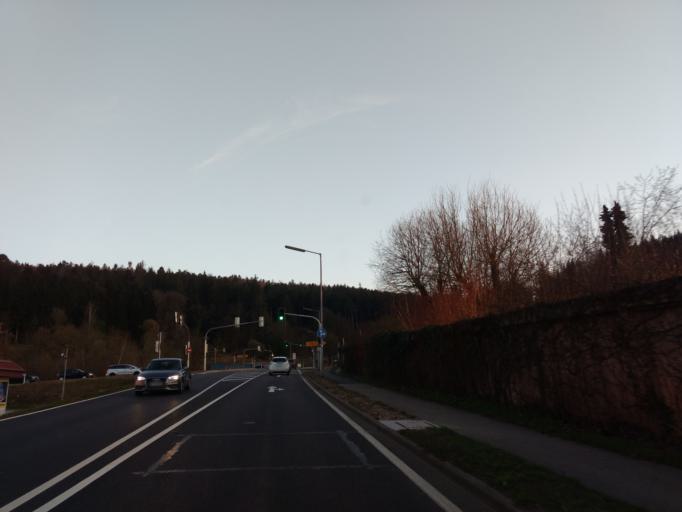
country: DE
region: Baden-Wuerttemberg
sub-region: Regierungsbezirk Stuttgart
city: Lorch
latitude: 48.7943
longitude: 9.7031
